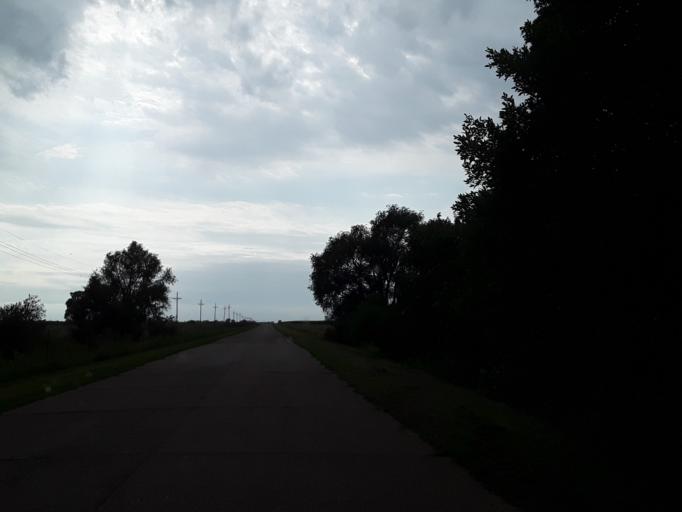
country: US
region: Nebraska
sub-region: Saunders County
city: Yutan
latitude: 41.1613
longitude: -96.4395
